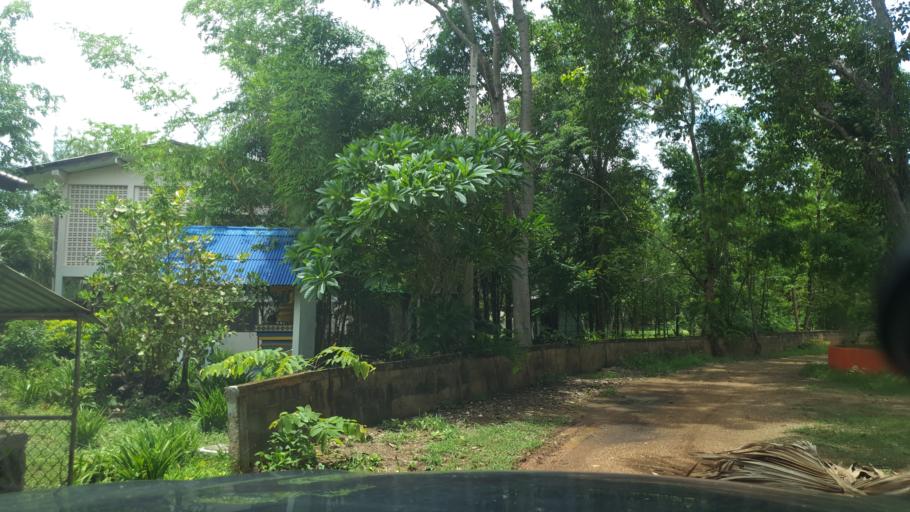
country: TH
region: Lampang
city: Ko Kha
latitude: 18.1977
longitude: 99.3293
